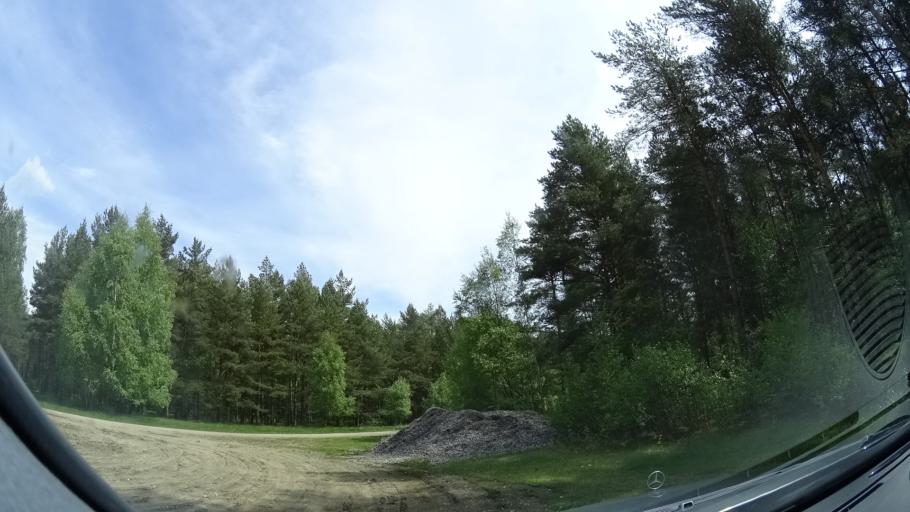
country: SE
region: Skane
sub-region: Sjobo Kommun
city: Sjoebo
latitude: 55.6708
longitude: 13.6361
